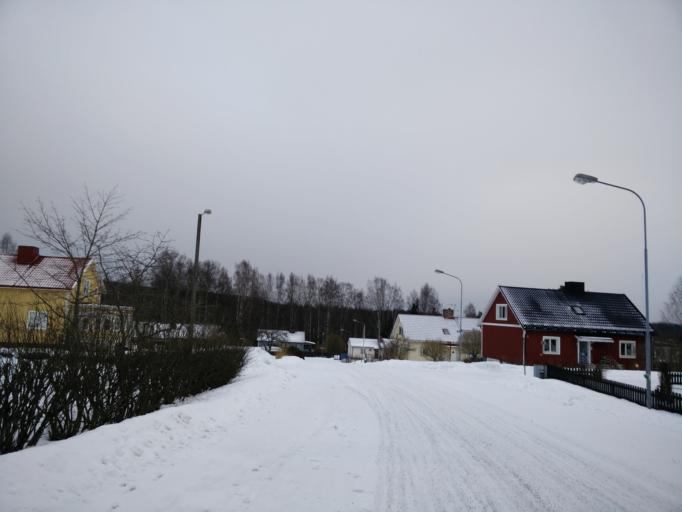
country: SE
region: Vaesternorrland
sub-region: Sundsvalls Kommun
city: Nolby
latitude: 62.2884
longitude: 17.3647
